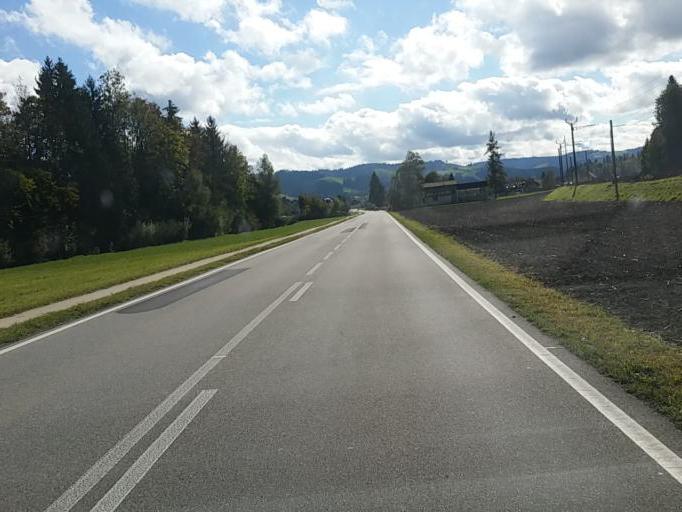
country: CH
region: Bern
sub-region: Emmental District
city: Ruderswil
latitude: 46.9972
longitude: 7.7252
